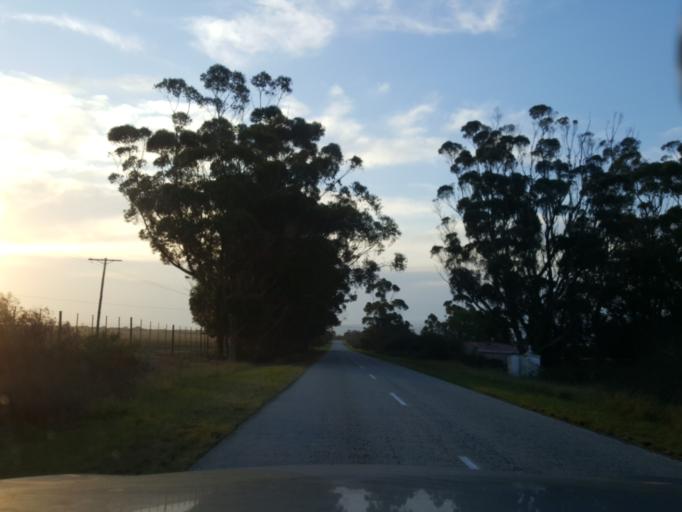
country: ZA
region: Eastern Cape
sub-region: Cacadu District Municipality
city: Grahamstown
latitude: -33.4467
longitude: 26.4862
